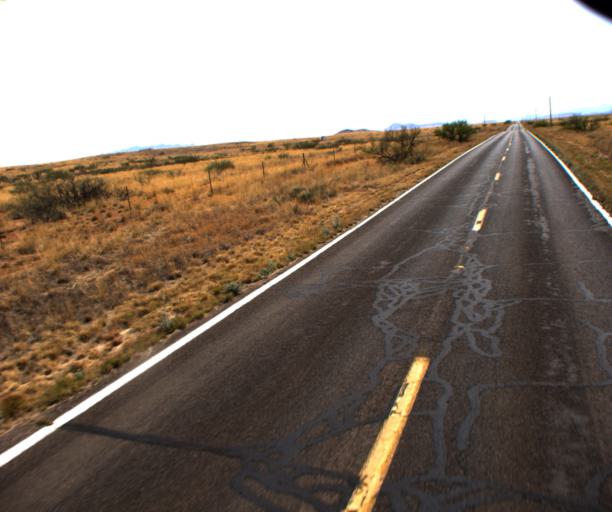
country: US
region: Arizona
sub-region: Cochise County
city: Willcox
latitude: 31.9830
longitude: -109.4589
